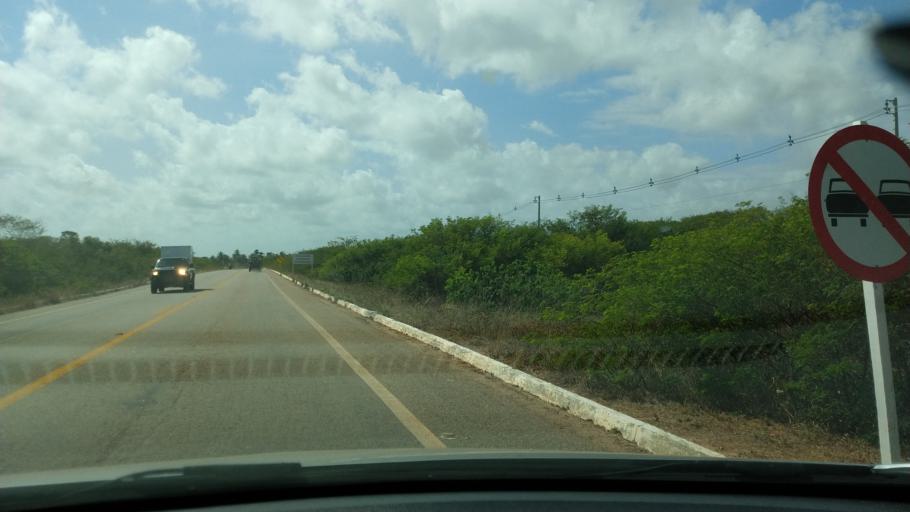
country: BR
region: Rio Grande do Norte
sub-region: Touros
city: Touros
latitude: -5.1995
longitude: -35.5008
